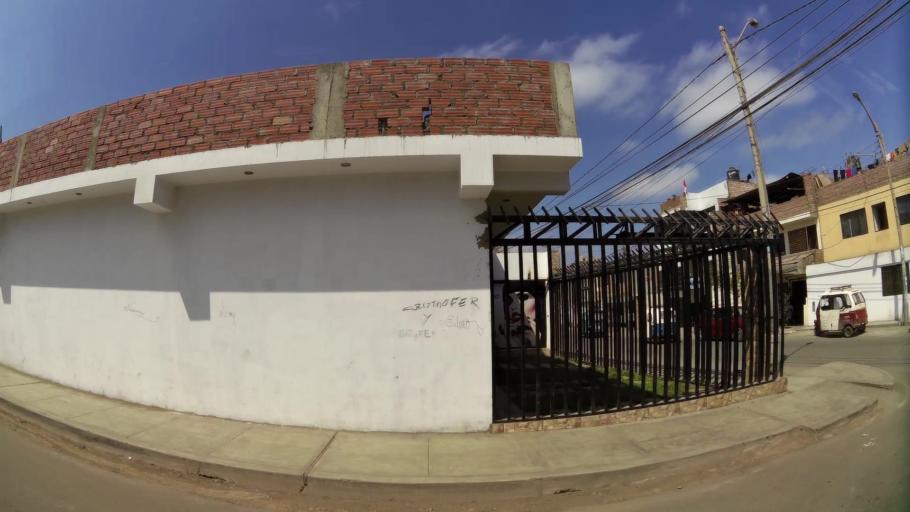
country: PE
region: Lima
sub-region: Provincia de Canete
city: Mala
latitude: -12.6614
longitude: -76.6307
